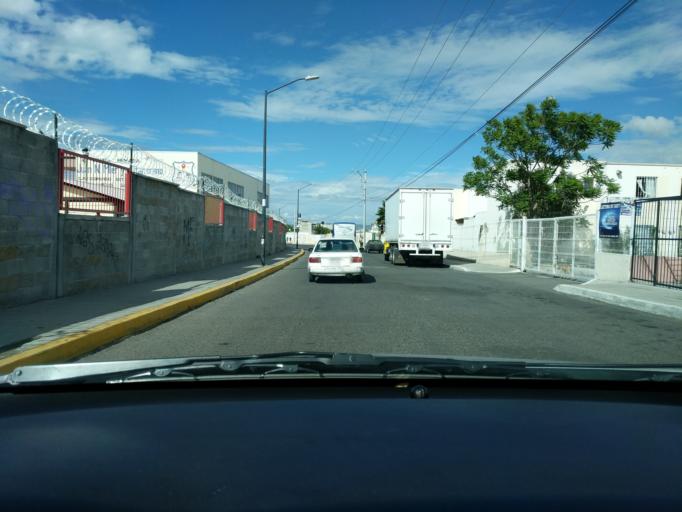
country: MX
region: Queretaro
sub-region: El Marques
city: Paseos del Marques
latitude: 20.6030
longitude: -100.2390
